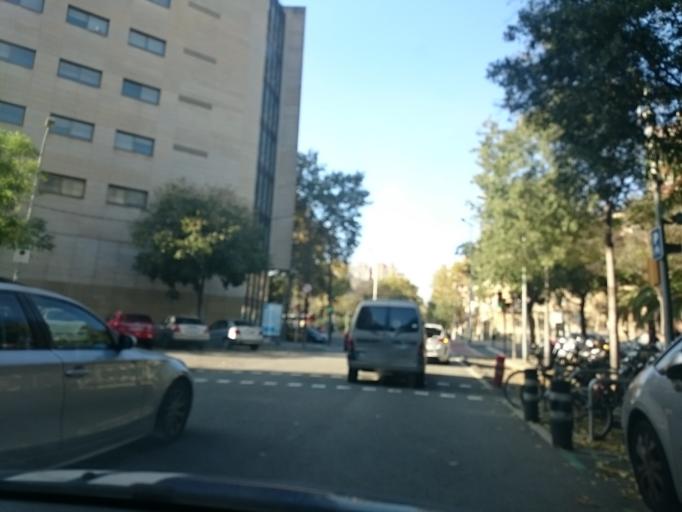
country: ES
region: Catalonia
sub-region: Provincia de Barcelona
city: Horta-Guinardo
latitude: 41.4018
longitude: 2.1824
